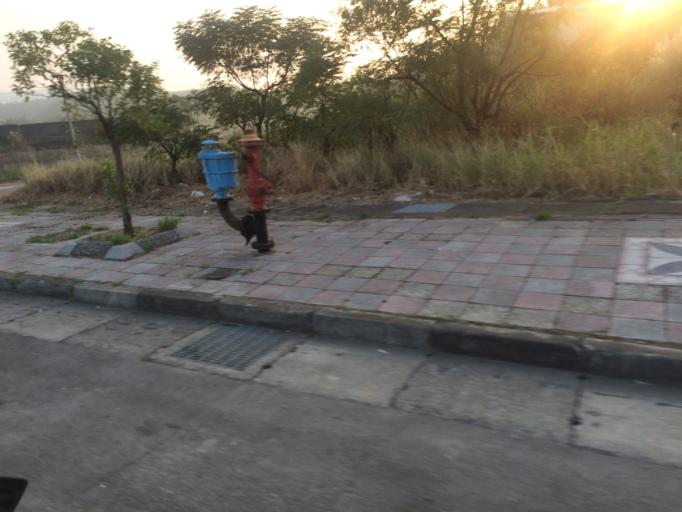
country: TW
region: Taiwan
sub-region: Hsinchu
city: Hsinchu
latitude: 24.7304
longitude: 120.9166
